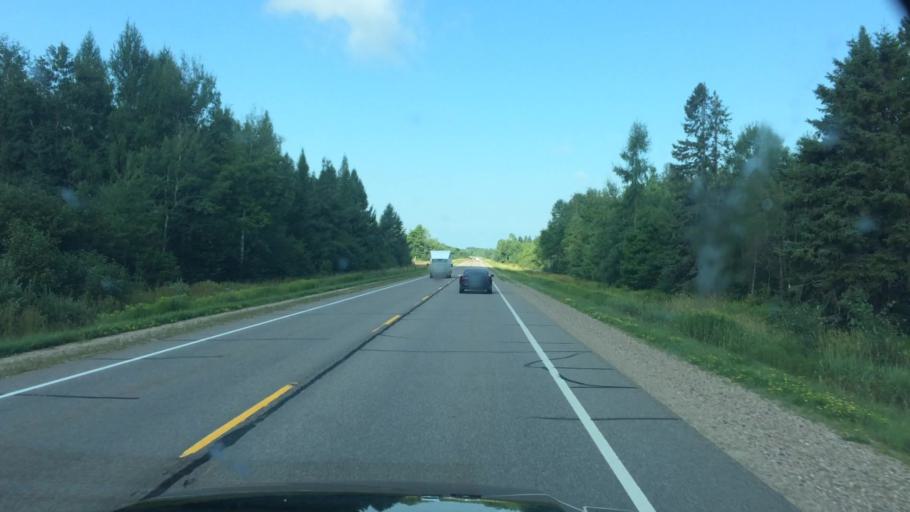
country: US
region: Wisconsin
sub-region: Langlade County
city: Antigo
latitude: 45.1459
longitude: -89.3240
